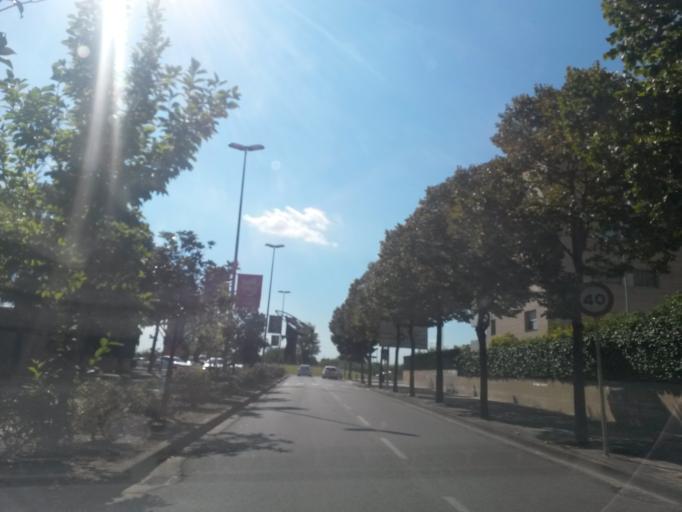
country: ES
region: Catalonia
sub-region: Provincia de Girona
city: Salt
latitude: 41.9679
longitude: 2.7873
